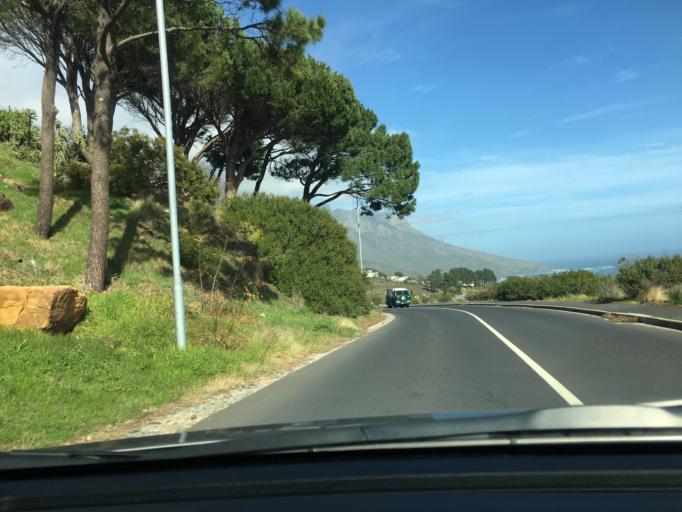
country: ZA
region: Western Cape
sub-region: City of Cape Town
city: Cape Town
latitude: -33.9549
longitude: 18.3859
